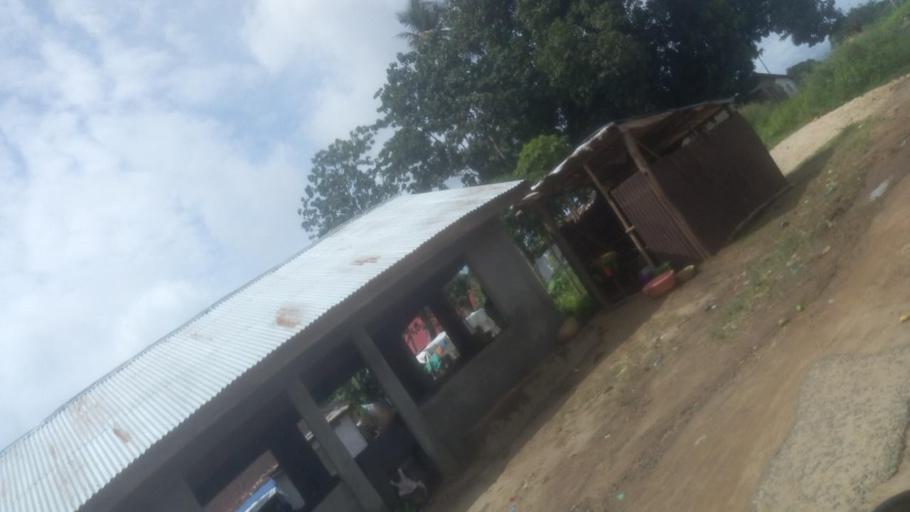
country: SL
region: Northern Province
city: Masoyila
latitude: 8.5891
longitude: -13.1995
